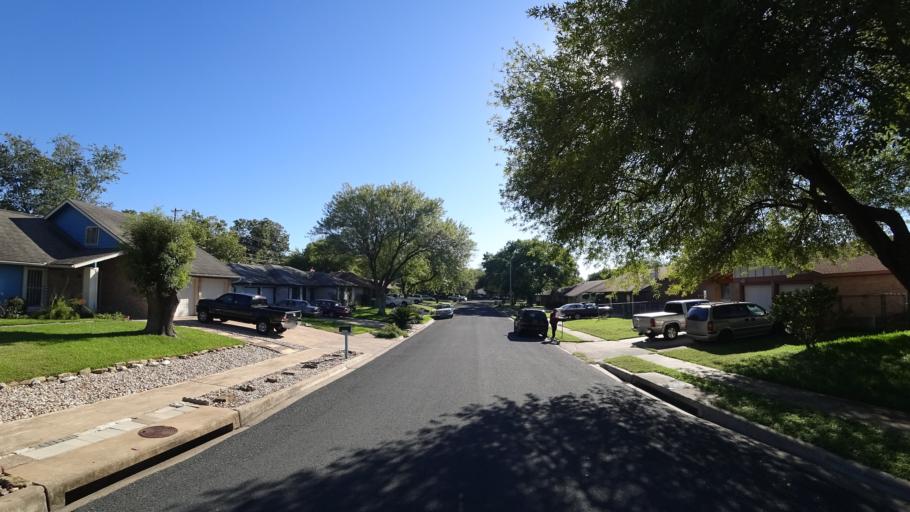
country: US
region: Texas
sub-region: Travis County
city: Austin
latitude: 30.2893
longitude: -97.6757
